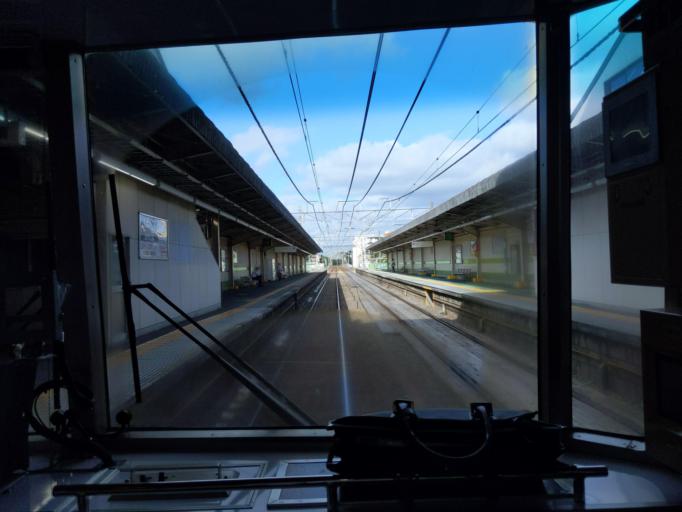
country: JP
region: Chiba
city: Funabashi
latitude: 35.7378
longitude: 140.0261
